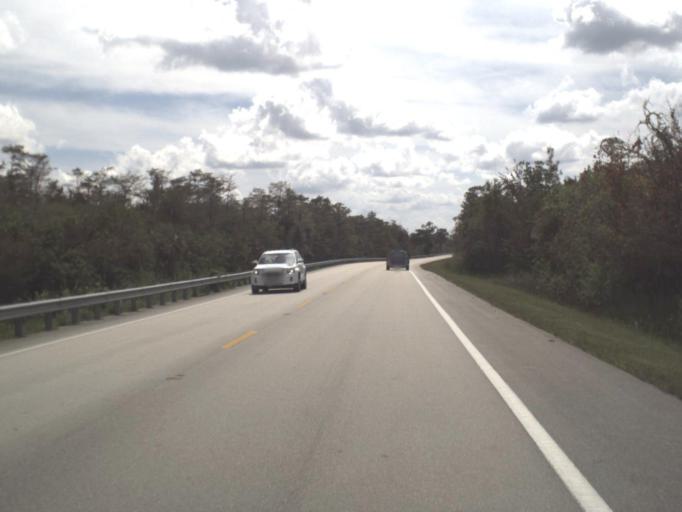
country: US
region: Florida
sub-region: Collier County
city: Lely Resort
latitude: 25.9408
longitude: -81.3574
